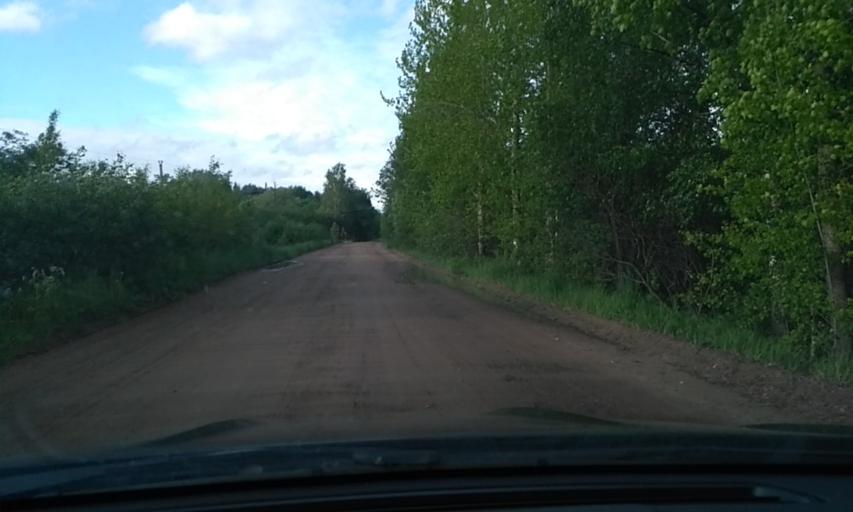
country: RU
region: Leningrad
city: Otradnoye
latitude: 59.8058
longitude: 30.8065
